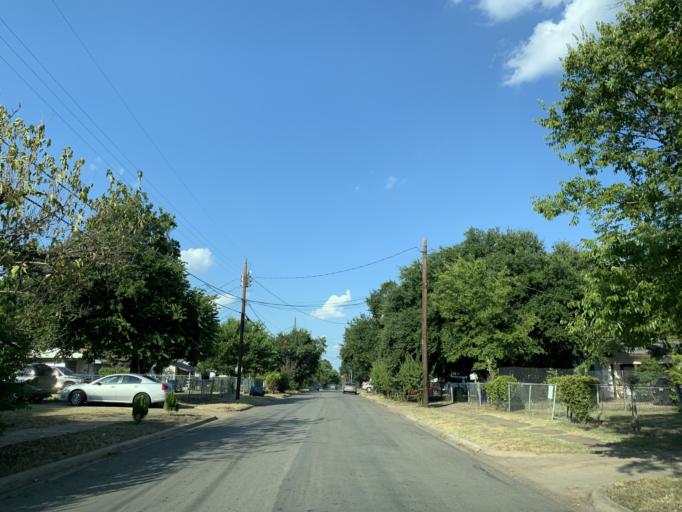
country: US
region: Texas
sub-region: Dallas County
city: Hutchins
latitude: 32.6969
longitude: -96.7799
